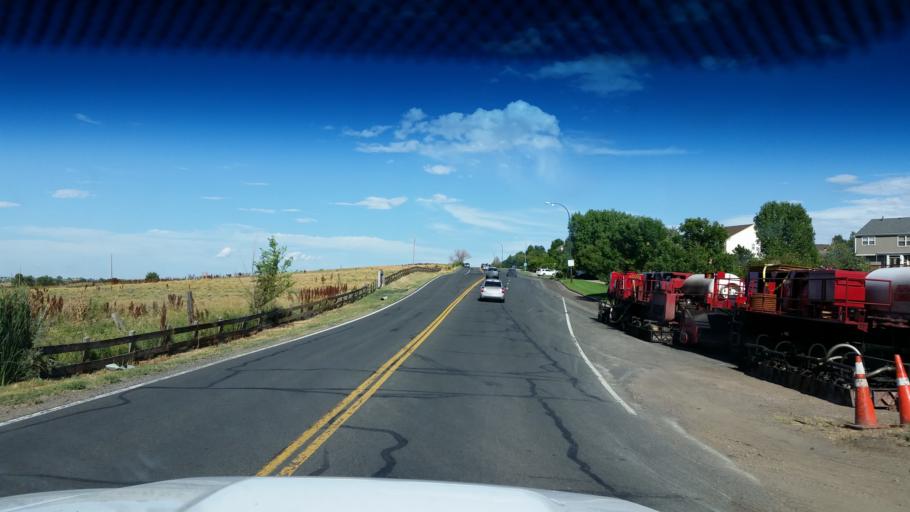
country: US
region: Colorado
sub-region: Adams County
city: Northglenn
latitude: 39.9286
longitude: -105.0063
